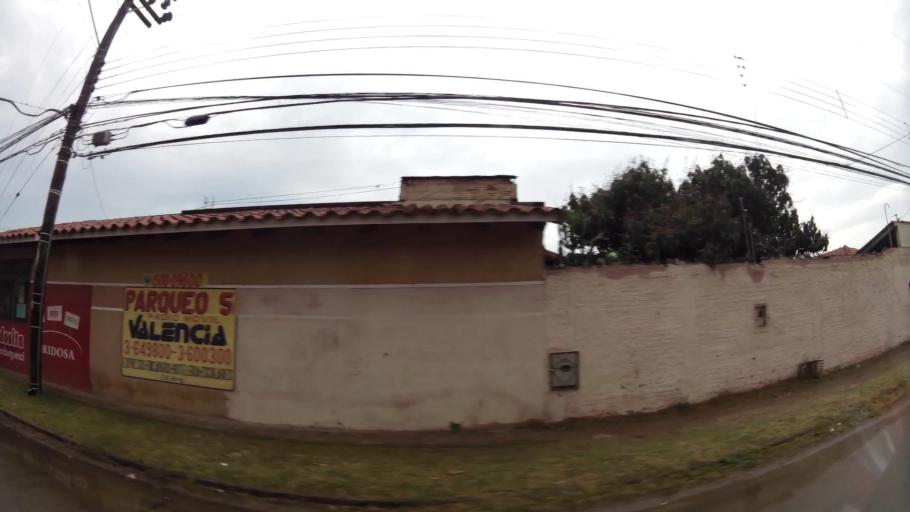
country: BO
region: Santa Cruz
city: Santa Cruz de la Sierra
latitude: -17.7788
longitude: -63.1337
